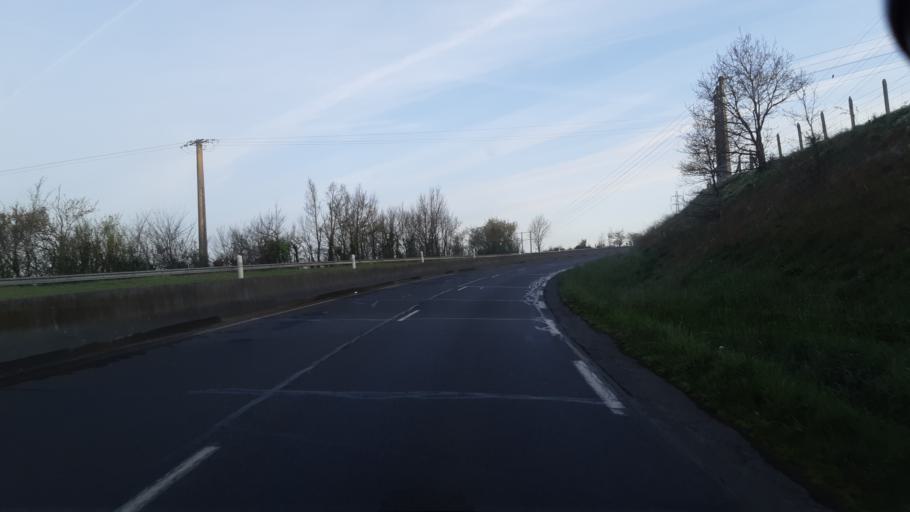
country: FR
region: Lower Normandy
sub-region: Departement de la Manche
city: Agneaux
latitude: 49.0951
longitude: -1.1211
